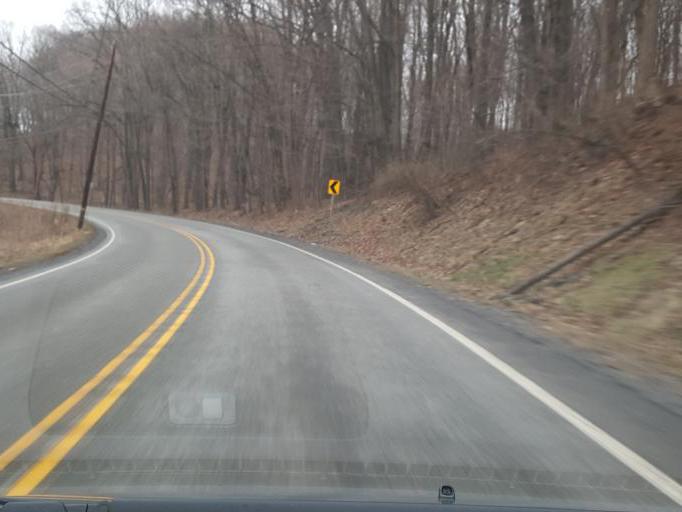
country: US
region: Pennsylvania
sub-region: Blair County
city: Greenwood
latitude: 40.5523
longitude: -78.3608
